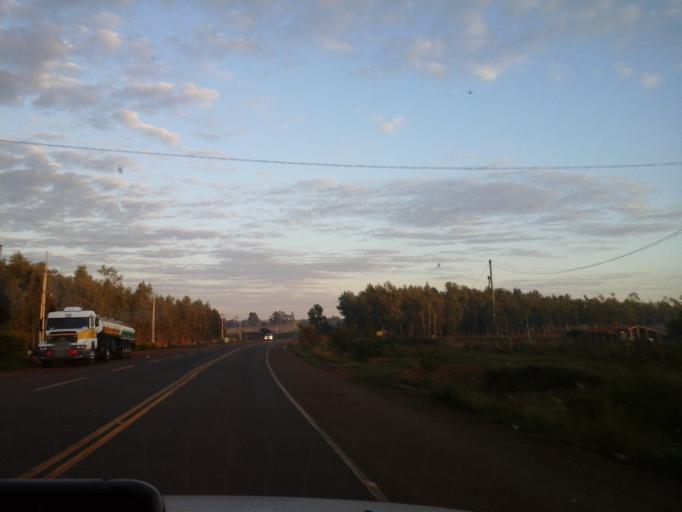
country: PY
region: Misiones
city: Santiago
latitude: -27.0431
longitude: -56.6584
